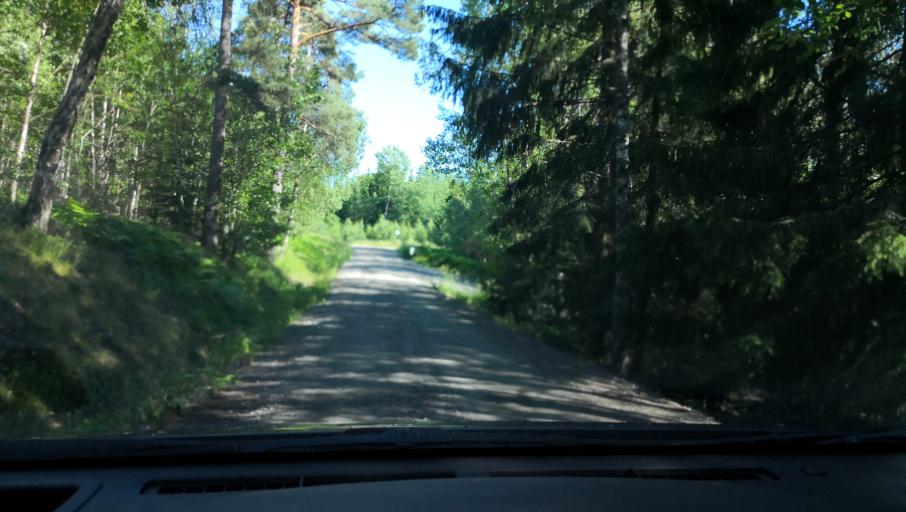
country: SE
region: Soedermanland
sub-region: Eskilstuna Kommun
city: Eskilstuna
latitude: 59.3284
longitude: 16.5842
